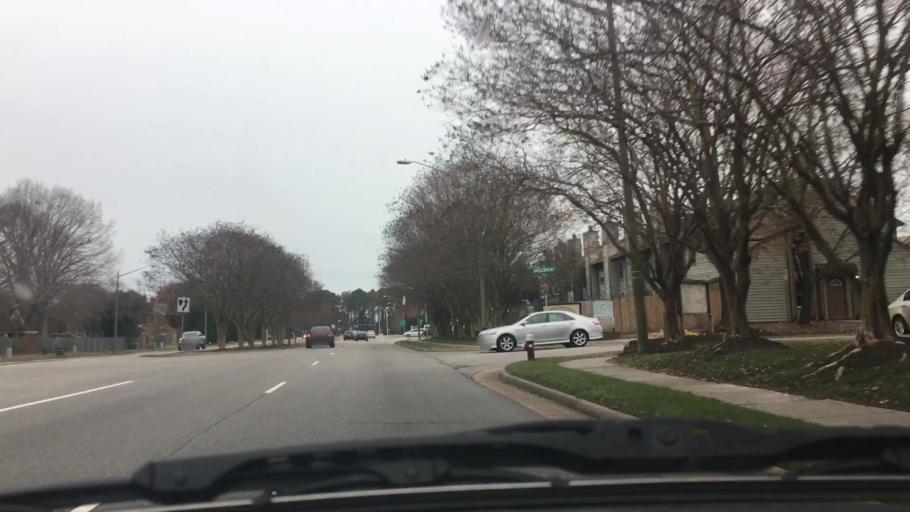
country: US
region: Virginia
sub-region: City of Chesapeake
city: Chesapeake
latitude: 36.8191
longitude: -76.1268
